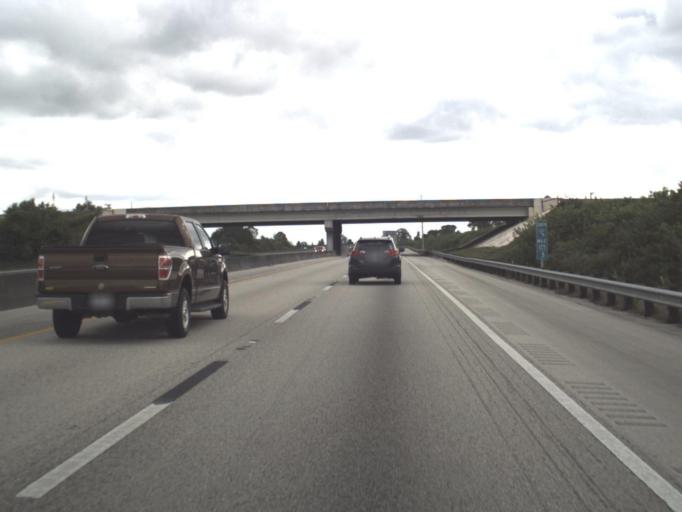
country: US
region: Florida
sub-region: Martin County
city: Hobe Sound
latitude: 27.0455
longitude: -80.2396
